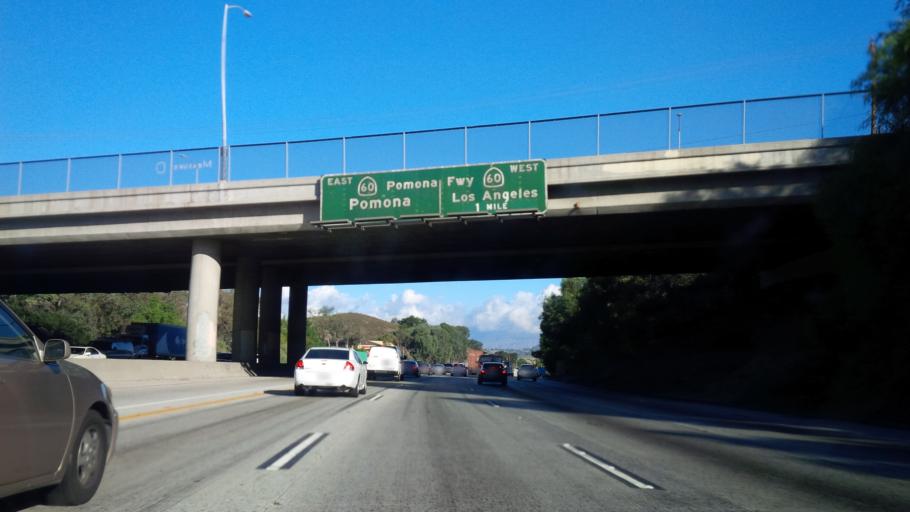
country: US
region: California
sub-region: Los Angeles County
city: Walnut
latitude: 33.9840
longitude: -117.8426
